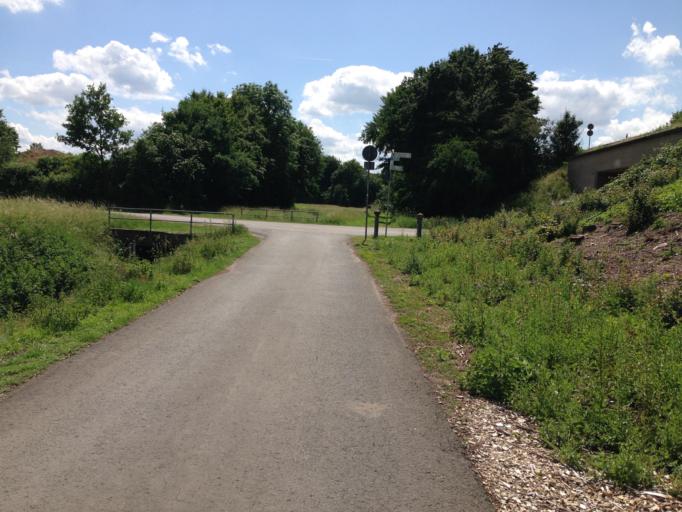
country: DE
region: Hesse
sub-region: Regierungsbezirk Giessen
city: Heuchelheim
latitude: 50.5711
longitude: 8.6439
